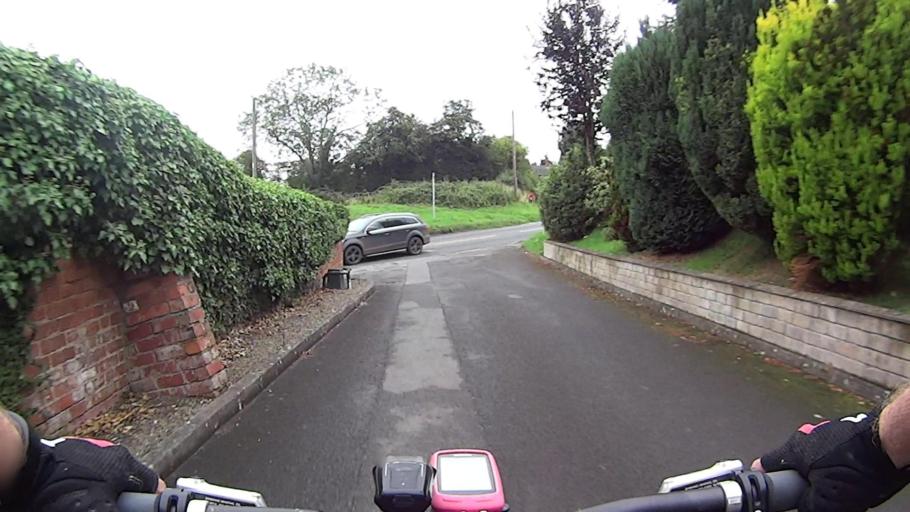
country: GB
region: England
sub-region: Worcestershire
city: Tenbury Wells
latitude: 52.2996
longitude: -2.5992
